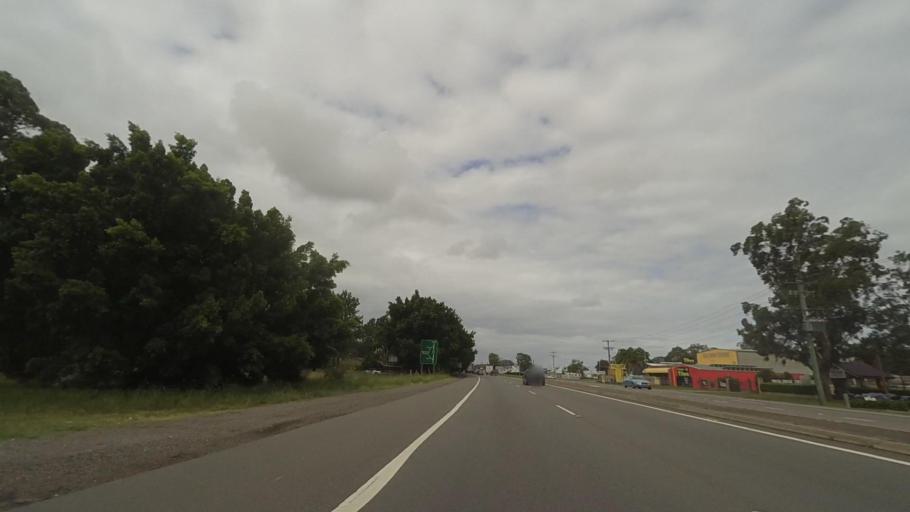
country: AU
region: New South Wales
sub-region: Port Stephens Shire
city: Raymond Terrace
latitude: -32.7871
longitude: 151.7299
